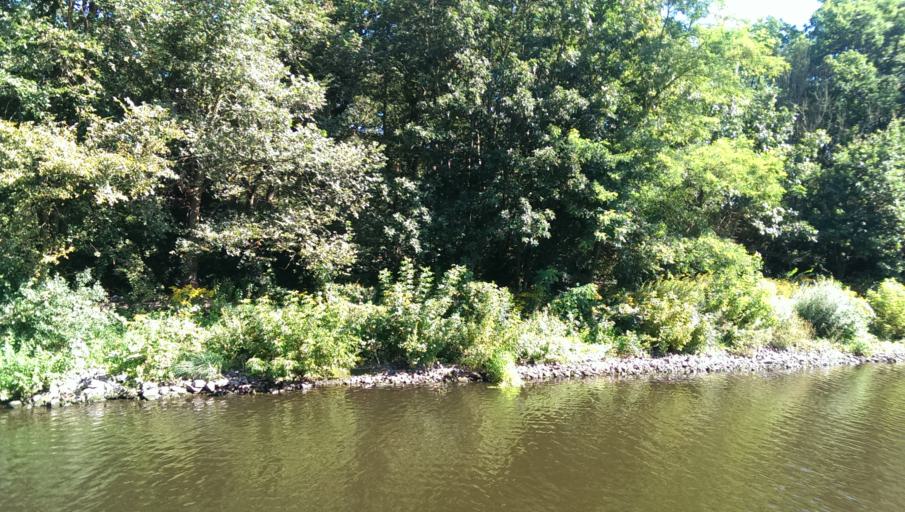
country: DE
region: Brandenburg
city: Stahnsdorf
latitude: 52.3980
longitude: 13.1920
